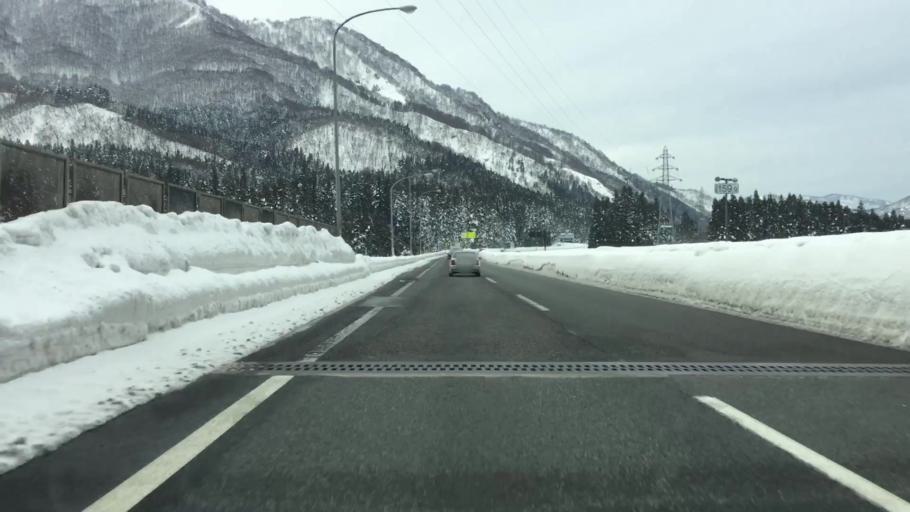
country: JP
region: Niigata
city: Shiozawa
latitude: 36.8796
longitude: 138.8562
